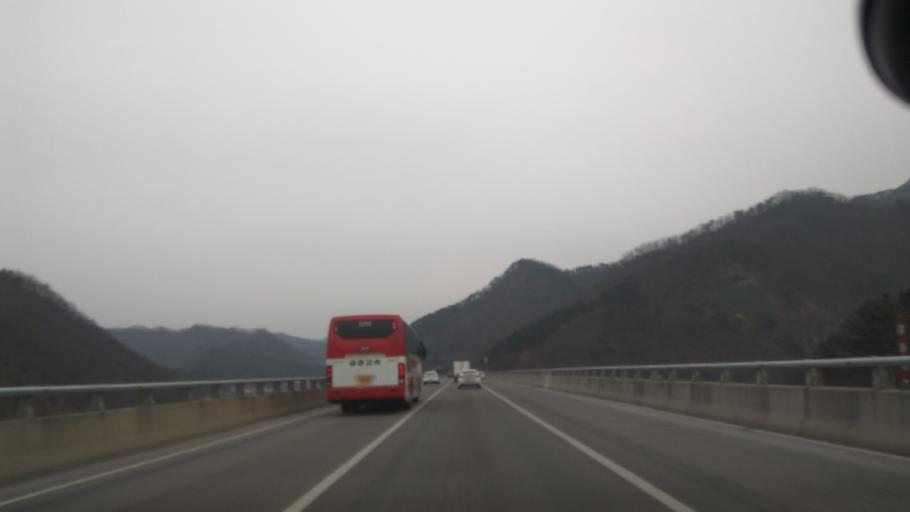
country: KR
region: Gyeonggi-do
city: Gapyeong
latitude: 37.7242
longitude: 127.5861
